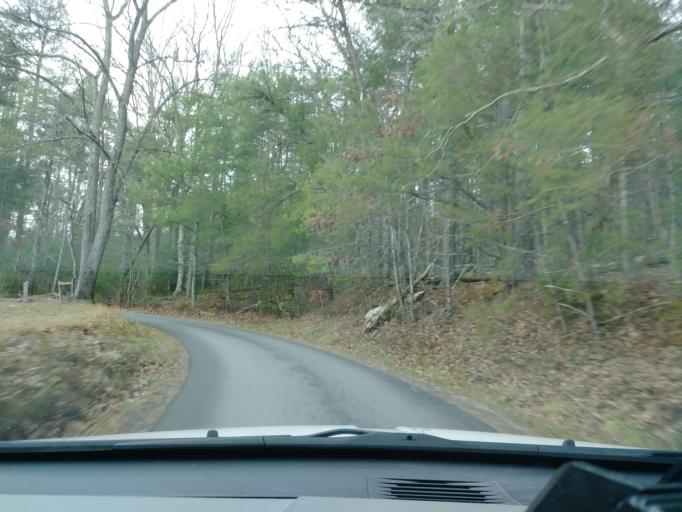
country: US
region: Tennessee
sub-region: Blount County
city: Wildwood
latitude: 35.6070
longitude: -83.8327
